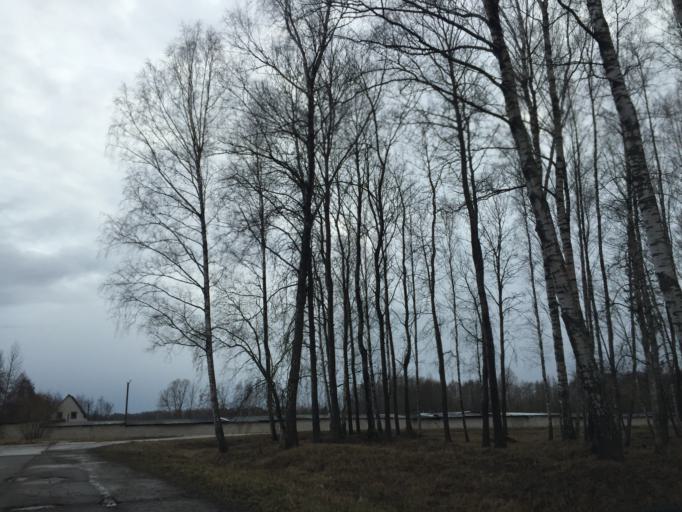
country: LV
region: Daugavpils
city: Daugavpils
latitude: 55.9378
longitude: 26.6532
